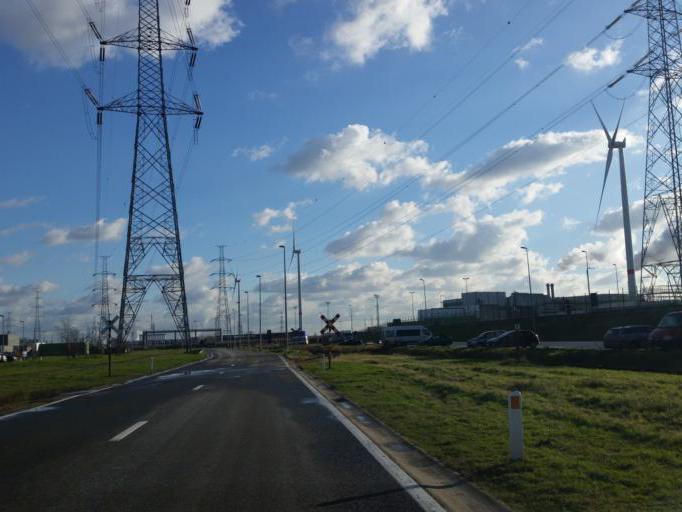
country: BE
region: Flanders
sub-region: Provincie Oost-Vlaanderen
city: Beveren
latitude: 51.2927
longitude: 4.2691
